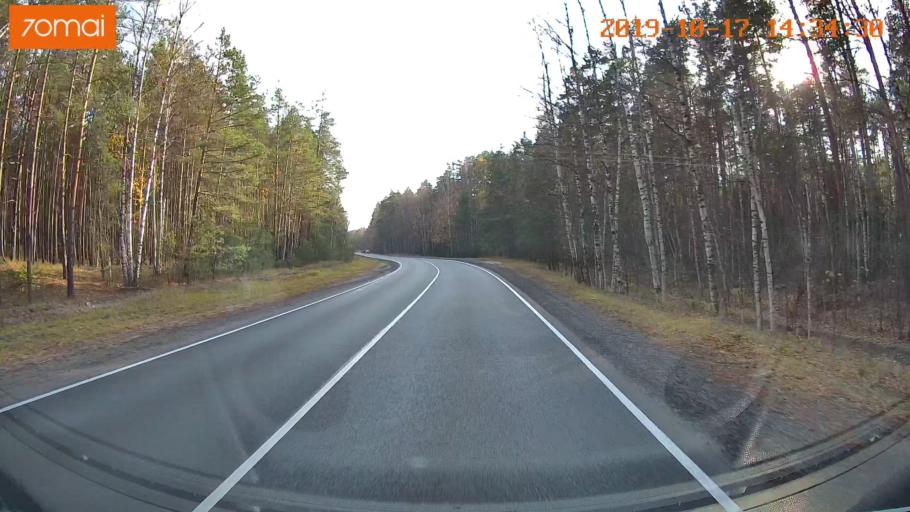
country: RU
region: Rjazan
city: Solotcha
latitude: 54.9116
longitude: 39.9977
